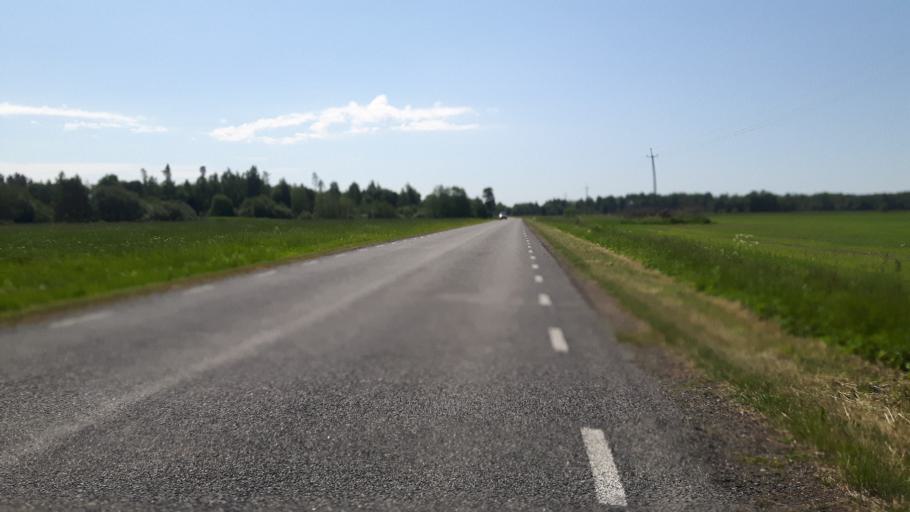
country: EE
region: Paernumaa
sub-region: Vaendra vald (alev)
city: Vandra
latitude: 58.6085
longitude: 25.0214
